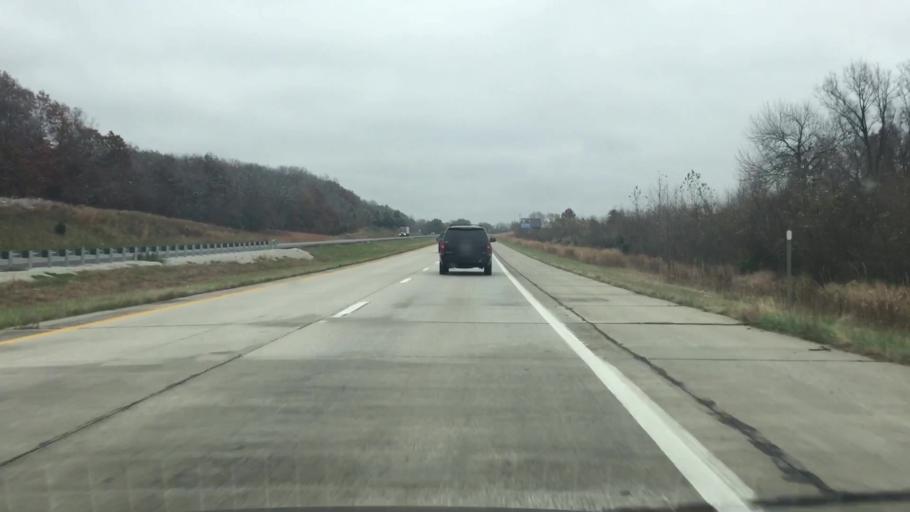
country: US
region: Missouri
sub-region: Saint Clair County
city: Osceola
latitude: 38.0177
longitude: -93.6651
